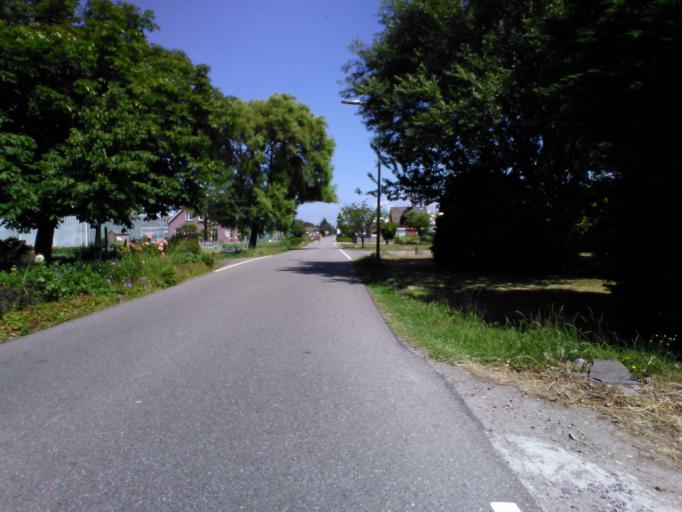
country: NL
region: South Holland
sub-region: Gemeente Westland
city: Maasdijk
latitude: 51.9543
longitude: 4.2061
